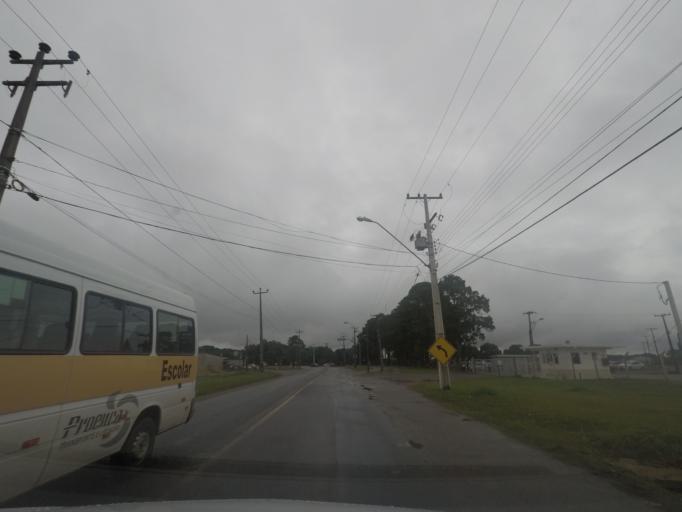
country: BR
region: Parana
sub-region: Quatro Barras
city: Quatro Barras
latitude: -25.3426
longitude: -49.0833
